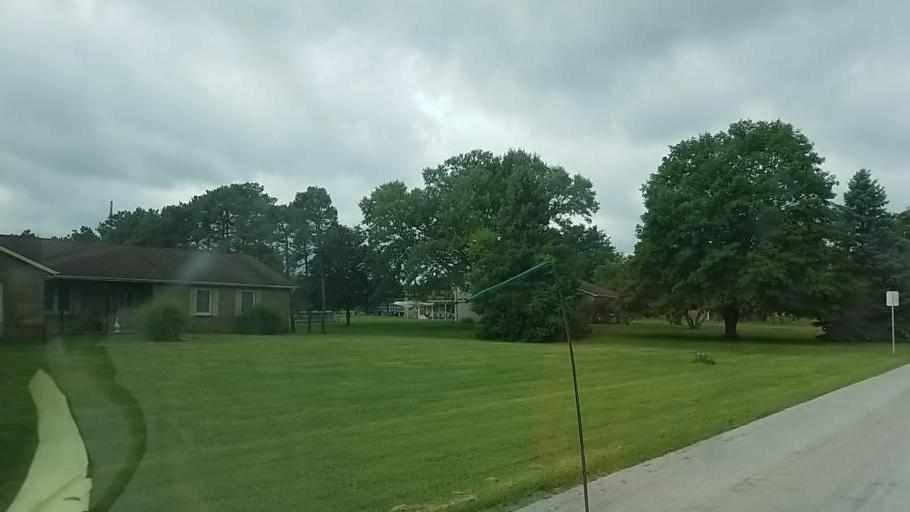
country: US
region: Ohio
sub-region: Pickaway County
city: Commercial Point
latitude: 39.8267
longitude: -83.0494
